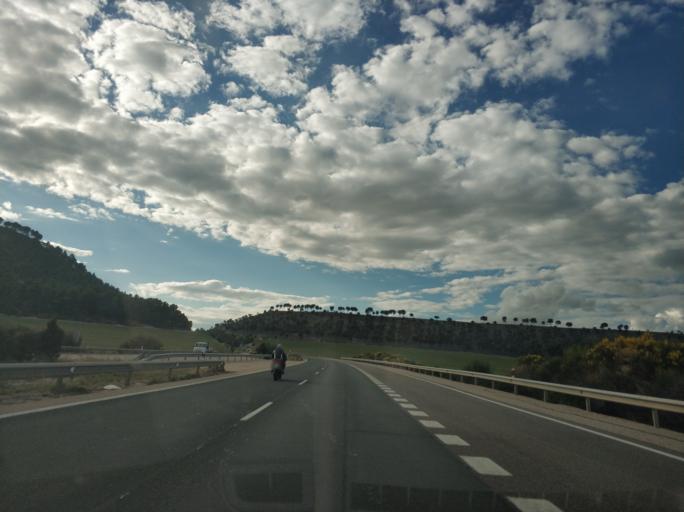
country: ES
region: Castille and Leon
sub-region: Provincia de Valladolid
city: Cisterniga
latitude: 41.6046
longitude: -4.6635
